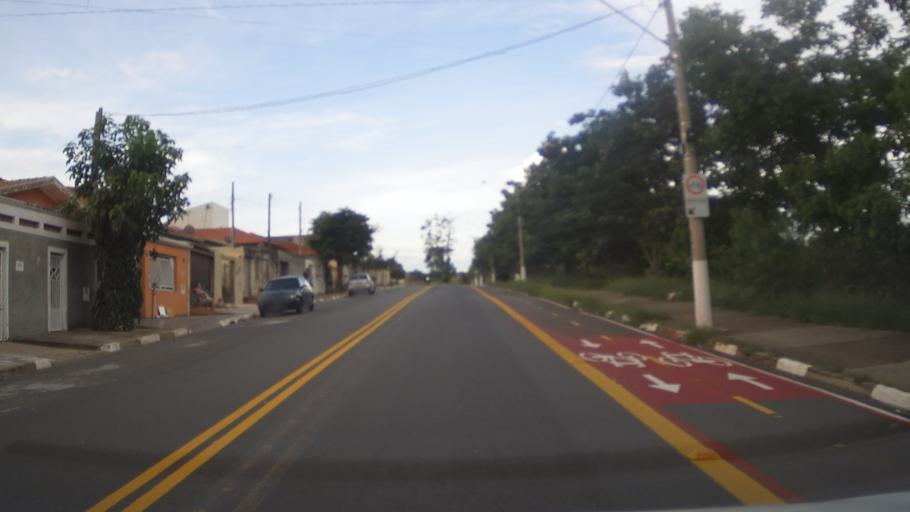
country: BR
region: Sao Paulo
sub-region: Hortolandia
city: Hortolandia
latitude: -22.9556
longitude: -47.1951
